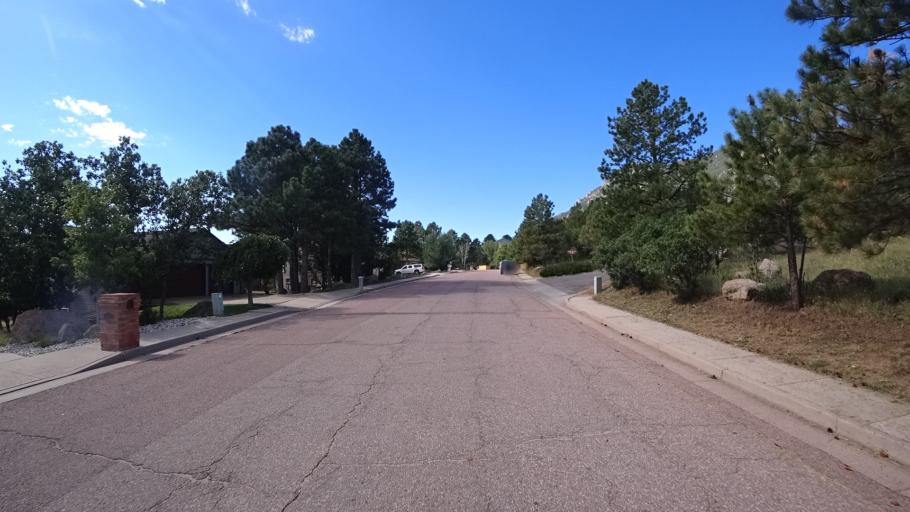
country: US
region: Colorado
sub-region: El Paso County
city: Fort Carson
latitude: 38.7596
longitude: -104.8318
